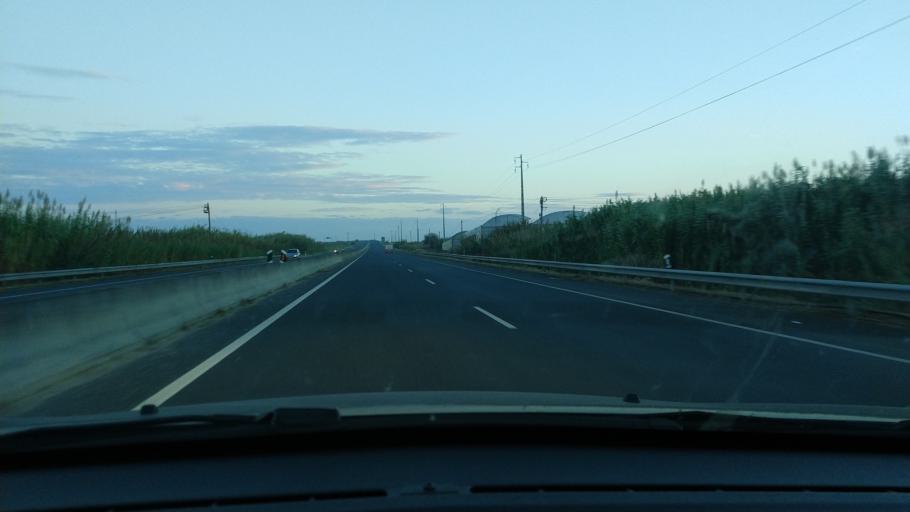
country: PT
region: Leiria
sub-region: Peniche
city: Atouguia da Baleia
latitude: 39.3417
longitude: -9.3391
